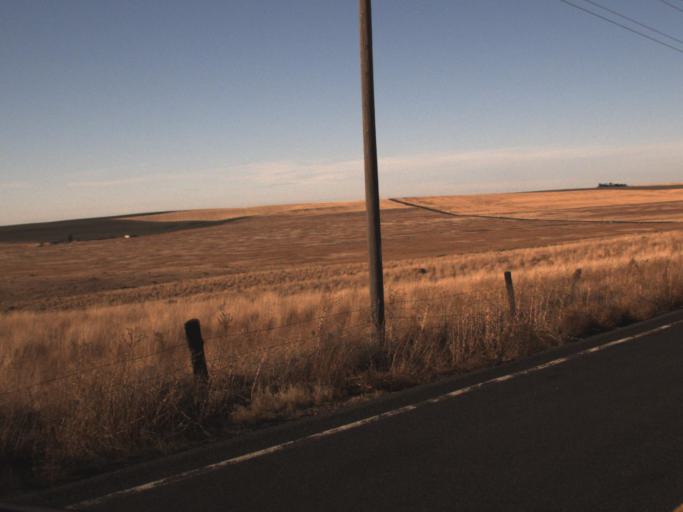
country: US
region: Washington
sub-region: Adams County
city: Ritzville
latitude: 47.0355
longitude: -118.3488
